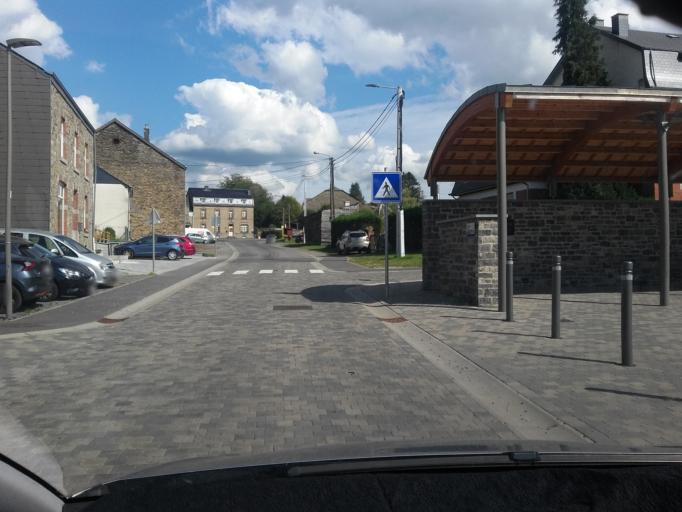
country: BE
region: Wallonia
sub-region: Province du Luxembourg
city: Saint-Hubert
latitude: 50.0326
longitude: 5.3208
